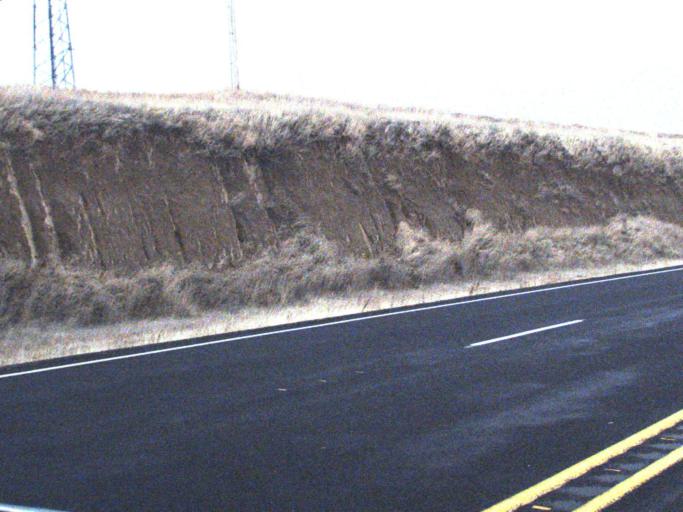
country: US
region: Washington
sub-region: Columbia County
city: Dayton
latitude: 46.3911
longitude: -117.9373
